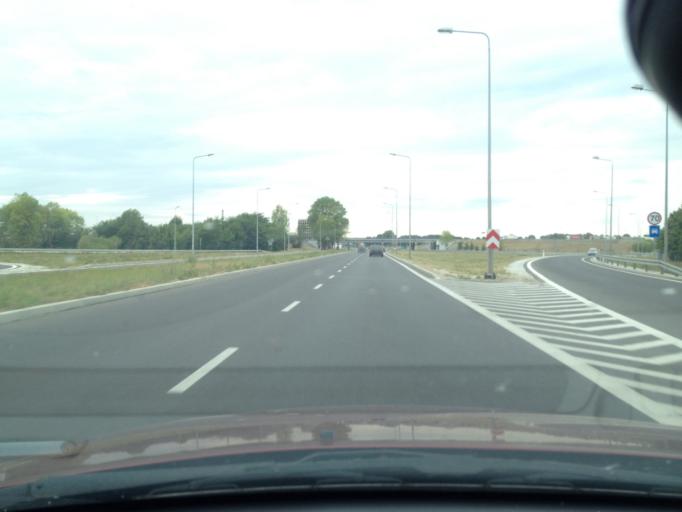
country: PL
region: Lubusz
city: Gorzow Wielkopolski
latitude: 52.7435
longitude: 15.1670
